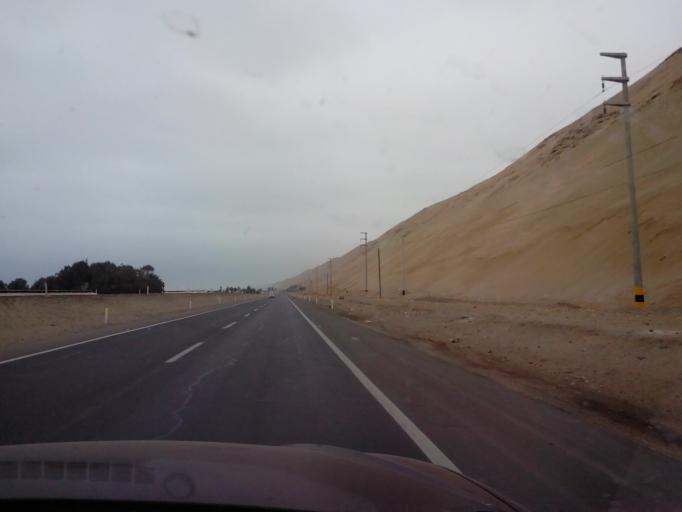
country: PE
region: Ica
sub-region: Provincia de Chincha
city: San Pedro
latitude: -13.3594
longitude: -76.2176
